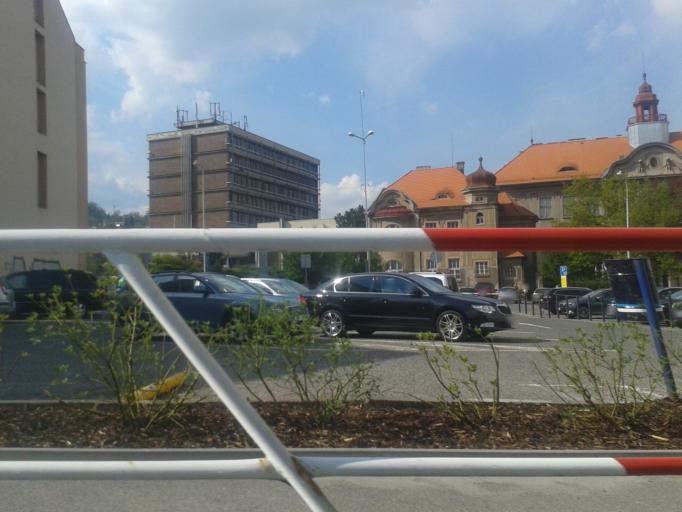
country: CZ
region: Central Bohemia
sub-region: Okres Beroun
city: Beroun
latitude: 49.9653
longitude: 14.0714
